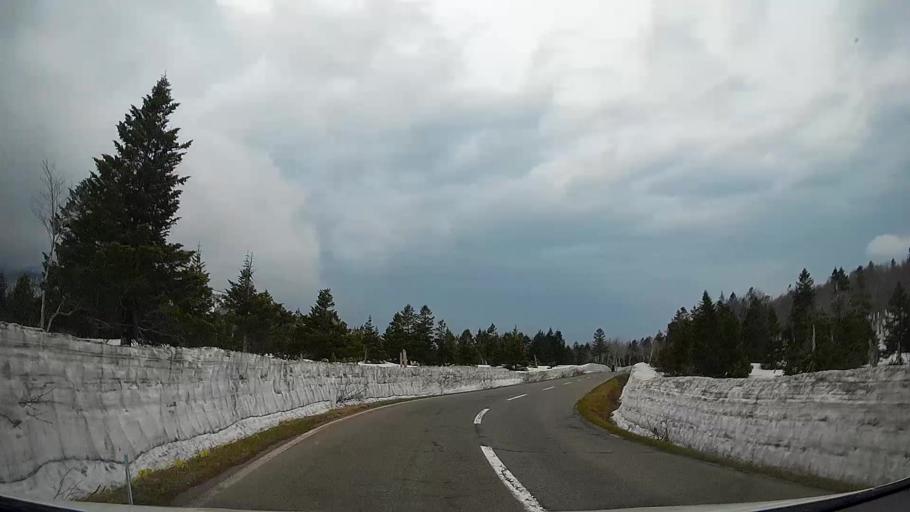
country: JP
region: Aomori
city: Aomori Shi
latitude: 40.6384
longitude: 140.8643
